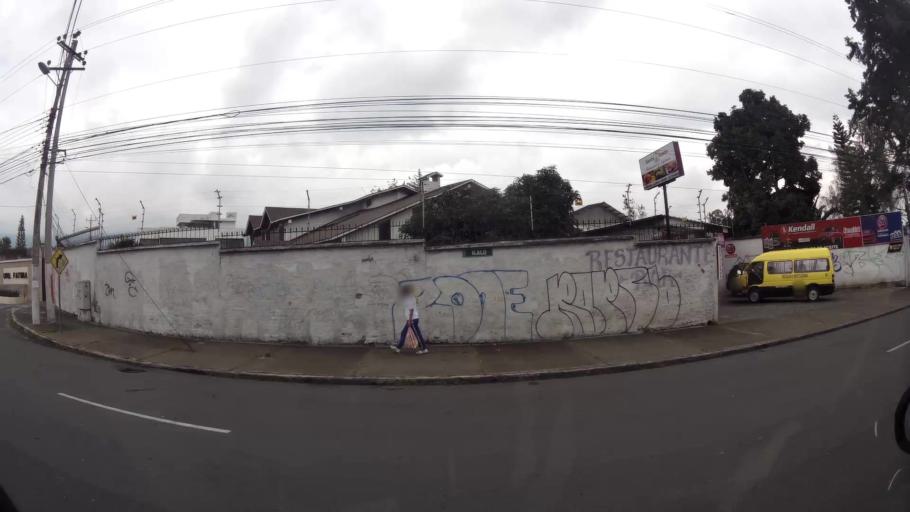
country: EC
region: Pichincha
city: Sangolqui
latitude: -0.3051
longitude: -78.4680
